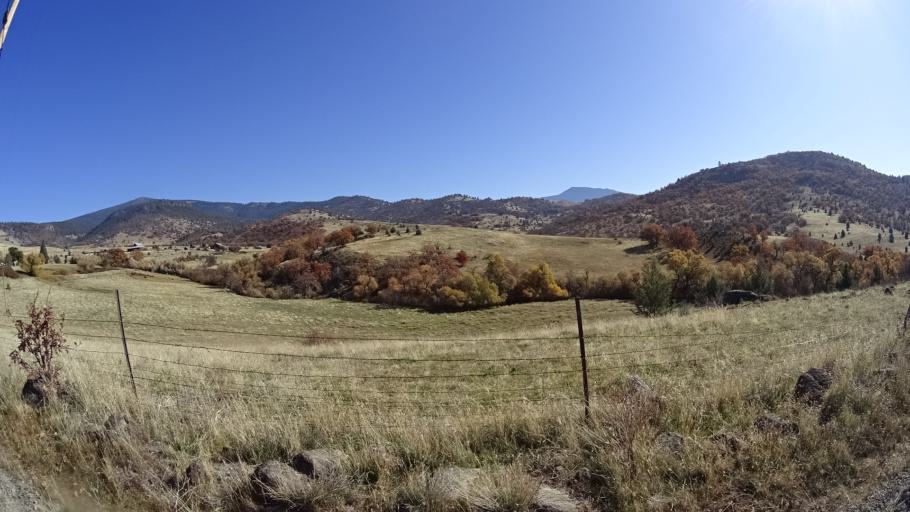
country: US
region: California
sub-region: Siskiyou County
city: Montague
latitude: 41.7978
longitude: -122.3352
